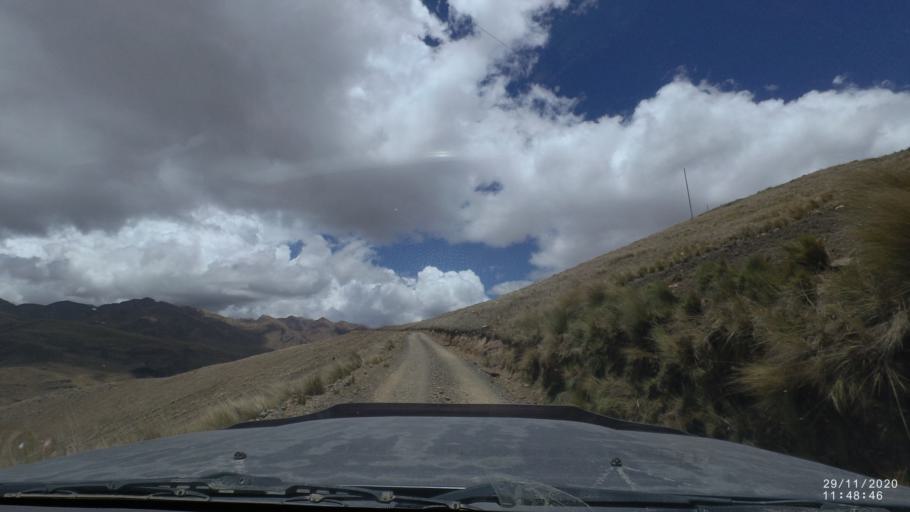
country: BO
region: Cochabamba
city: Cochabamba
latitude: -17.1778
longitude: -66.2580
